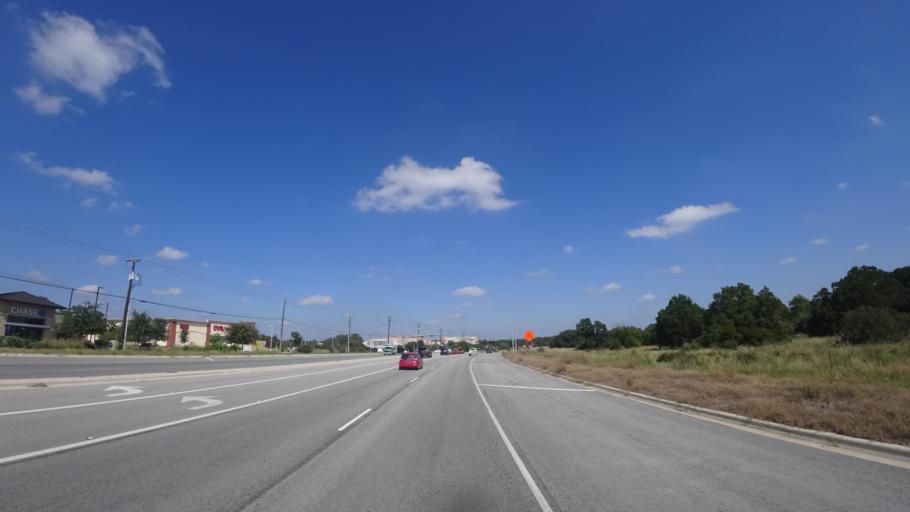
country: US
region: Texas
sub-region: Williamson County
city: Brushy Creek
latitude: 30.5061
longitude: -97.7167
